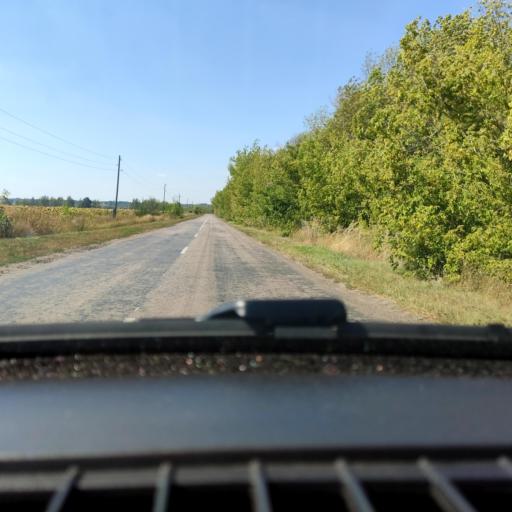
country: RU
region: Voronezj
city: Orlovo
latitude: 51.6429
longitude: 39.7414
